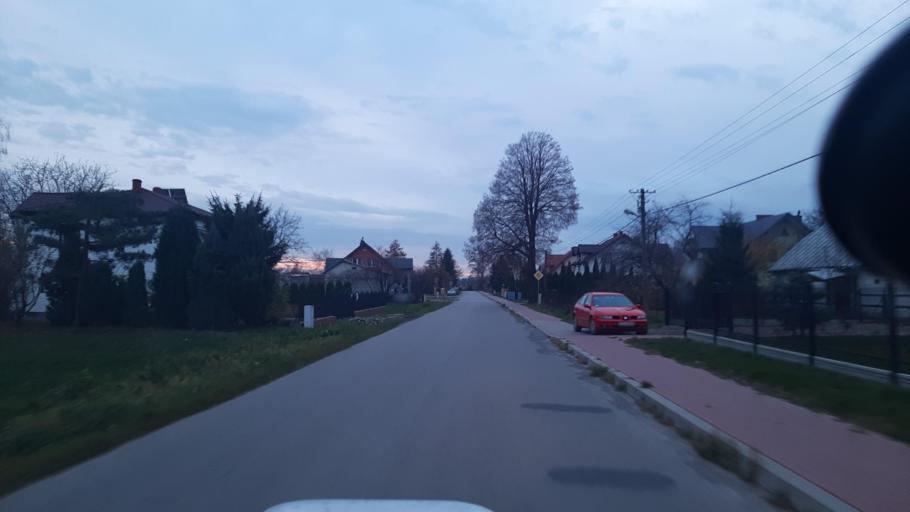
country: PL
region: Lublin Voivodeship
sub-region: Powiat lubelski
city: Garbow
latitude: 51.3604
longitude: 22.3763
